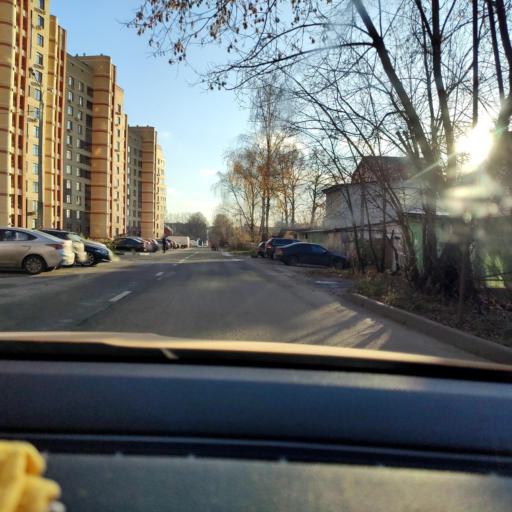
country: RU
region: Moscow
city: Yaroslavskiy
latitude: 55.8953
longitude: 37.7100
